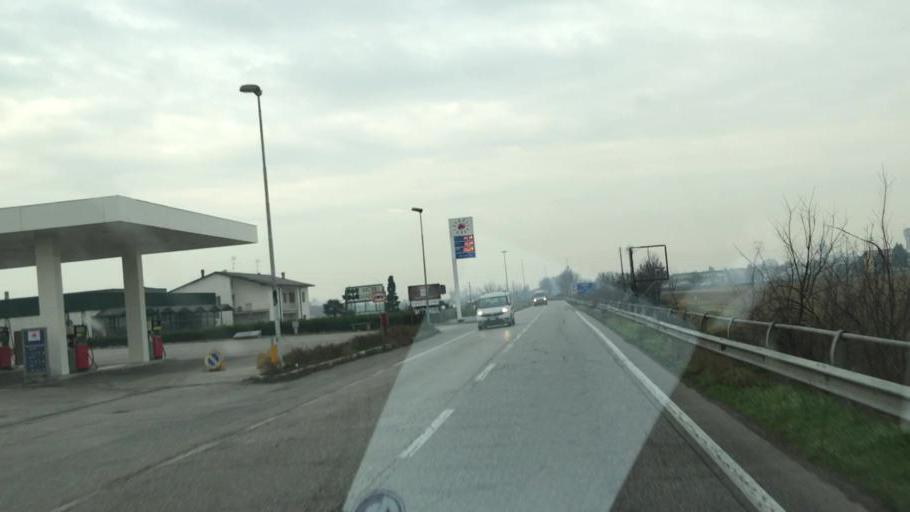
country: IT
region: Lombardy
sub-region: Provincia di Mantova
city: Asola
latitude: 45.2330
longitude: 10.4167
